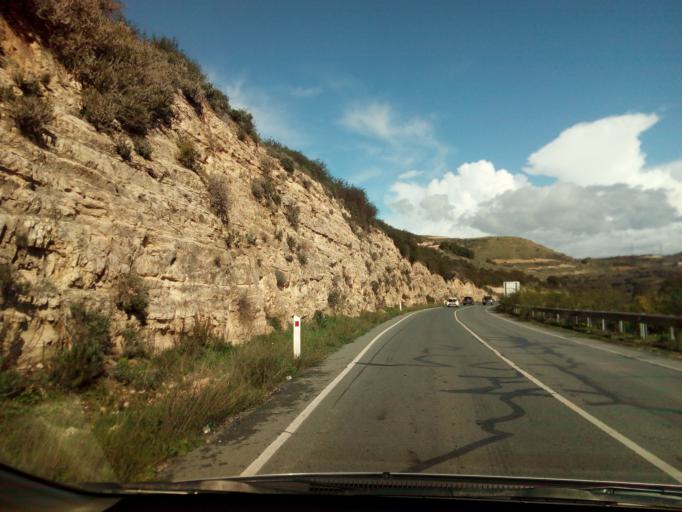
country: CY
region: Pafos
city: Mesogi
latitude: 34.8636
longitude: 32.4819
